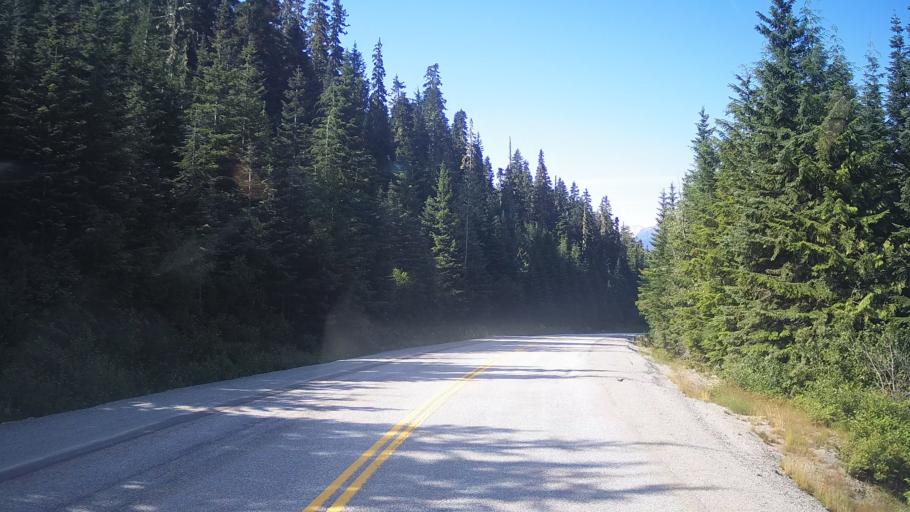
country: CA
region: British Columbia
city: Pemberton
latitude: 50.3608
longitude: -122.5228
